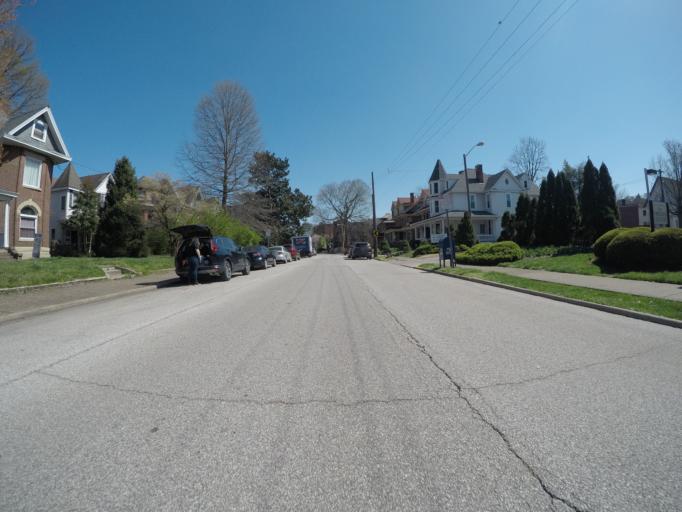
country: US
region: West Virginia
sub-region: Kanawha County
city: Charleston
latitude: 38.3422
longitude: -81.6268
